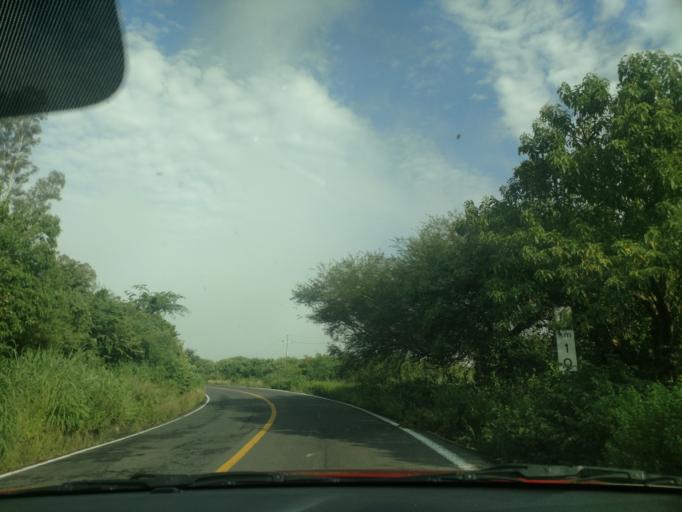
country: MX
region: Jalisco
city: Ameca
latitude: 20.5315
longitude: -104.1323
